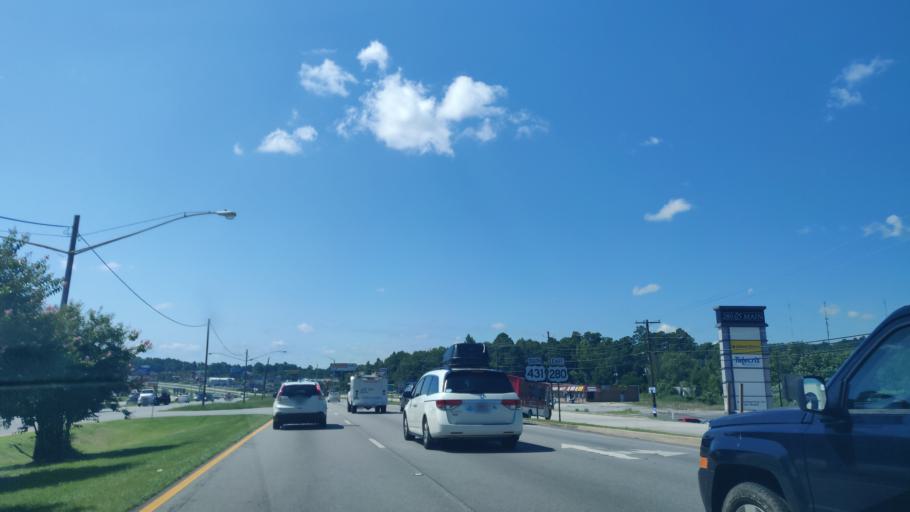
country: US
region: Alabama
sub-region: Russell County
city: Phenix City
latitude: 32.4745
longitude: -85.0301
